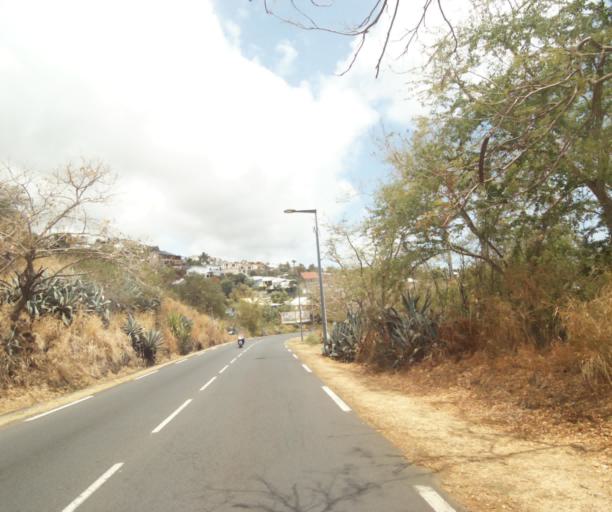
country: RE
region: Reunion
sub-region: Reunion
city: Saint-Paul
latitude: -21.0292
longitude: 55.2676
